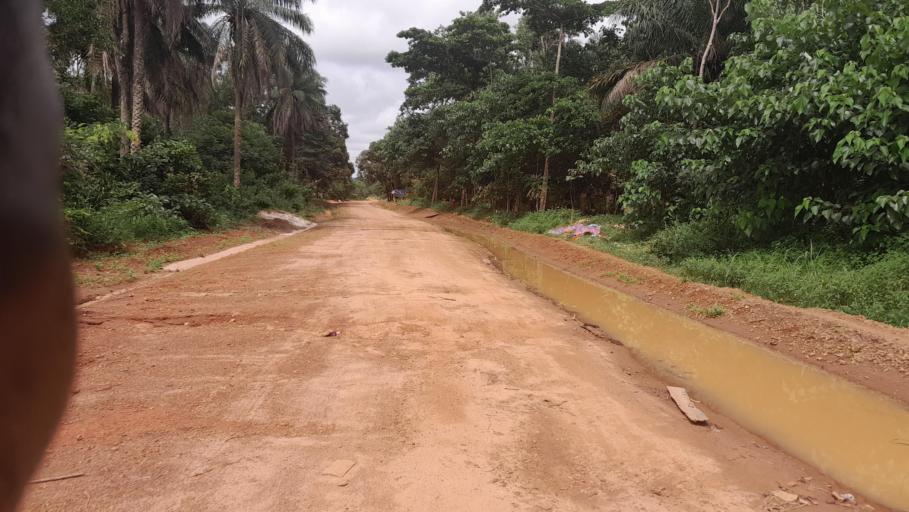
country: GN
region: Boke
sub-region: Boffa
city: Boffa
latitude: 10.0936
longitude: -13.8592
